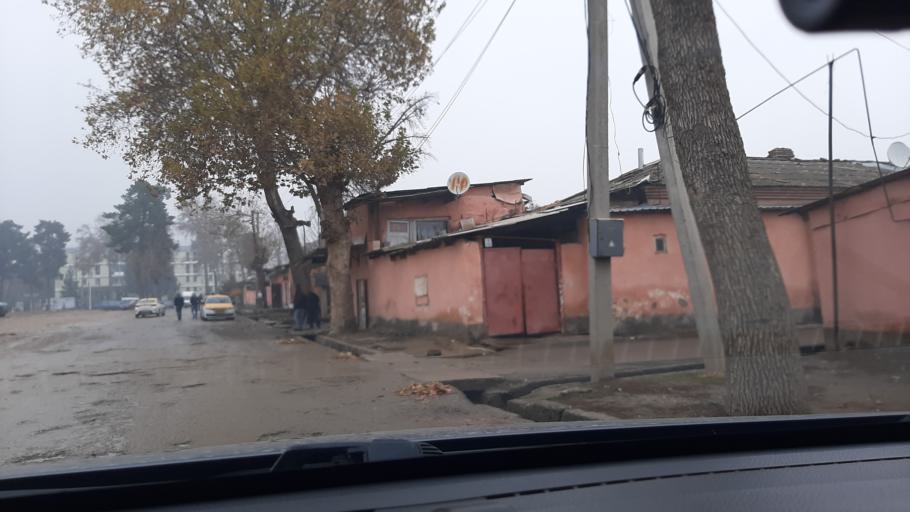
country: TJ
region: Dushanbe
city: Dushanbe
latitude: 38.5661
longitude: 68.8024
